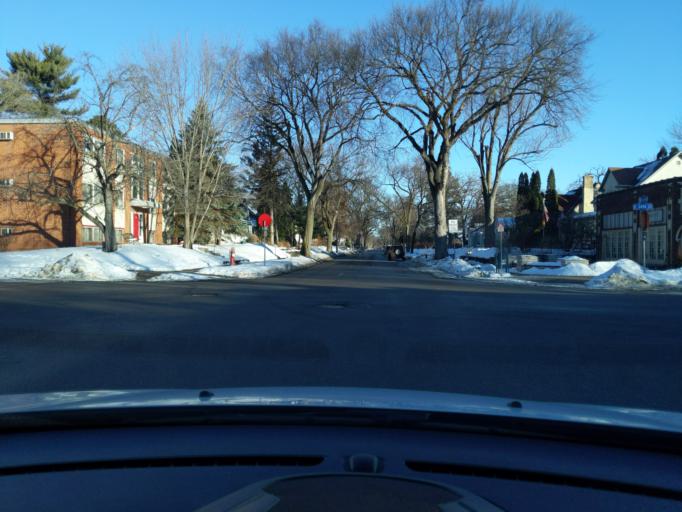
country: US
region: Minnesota
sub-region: Ramsey County
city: Lauderdale
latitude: 44.9414
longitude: -93.2127
